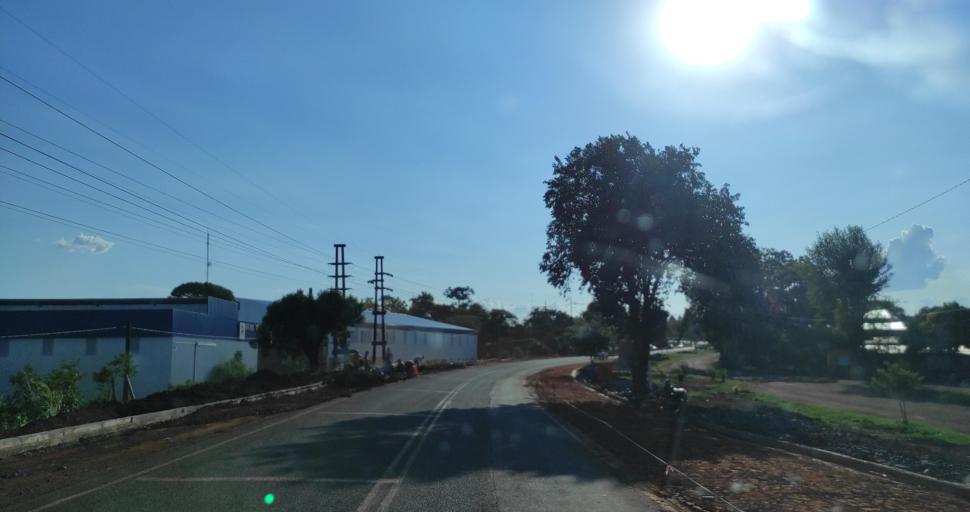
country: AR
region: Misiones
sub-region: Departamento de Eldorado
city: Eldorado
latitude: -26.4142
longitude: -54.4922
